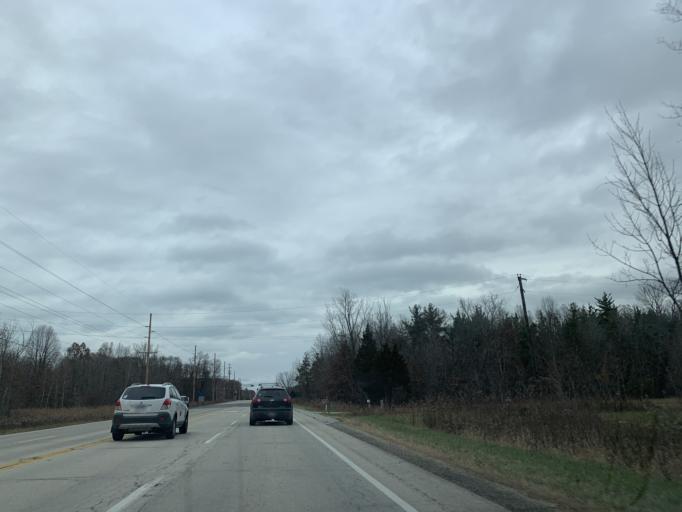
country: US
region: Indiana
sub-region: LaPorte County
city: Long Beach
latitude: 41.7283
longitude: -86.8261
